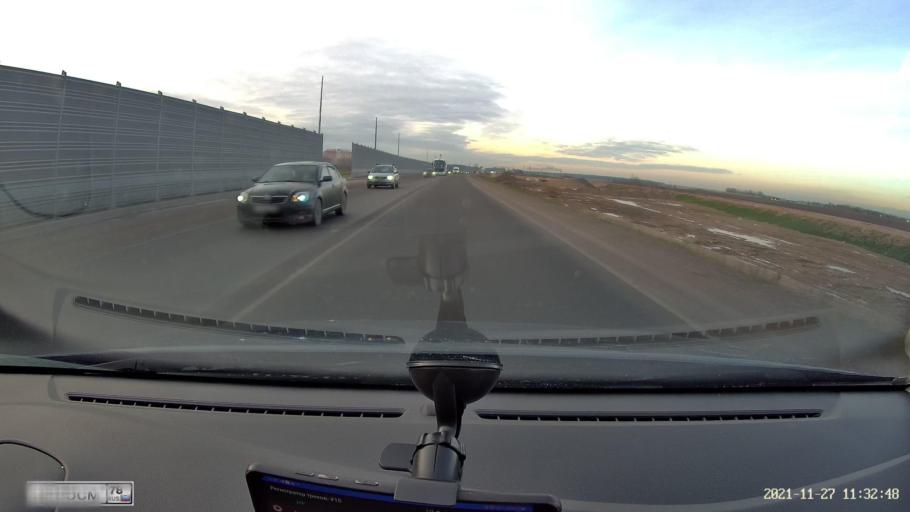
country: RU
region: Leningrad
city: Annino
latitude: 59.7124
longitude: 30.0280
